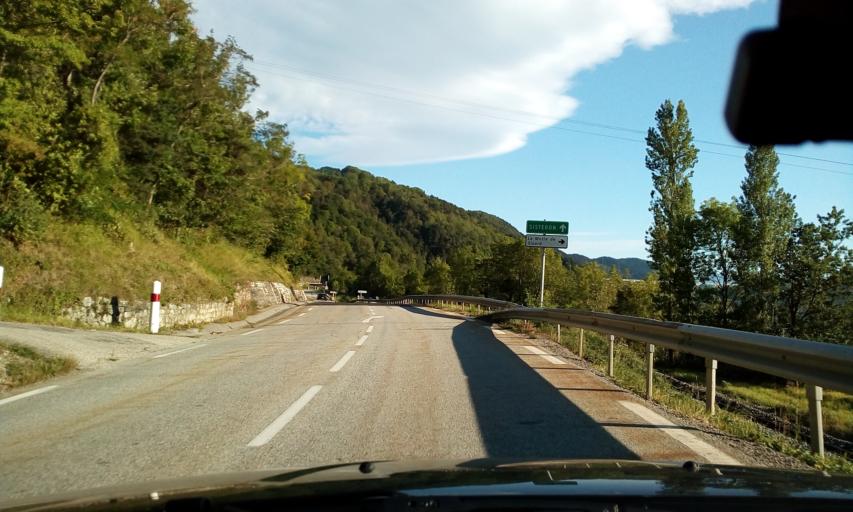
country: FR
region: Rhone-Alpes
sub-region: Departement de l'Isere
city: Le Gua
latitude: 44.9579
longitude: 5.6378
